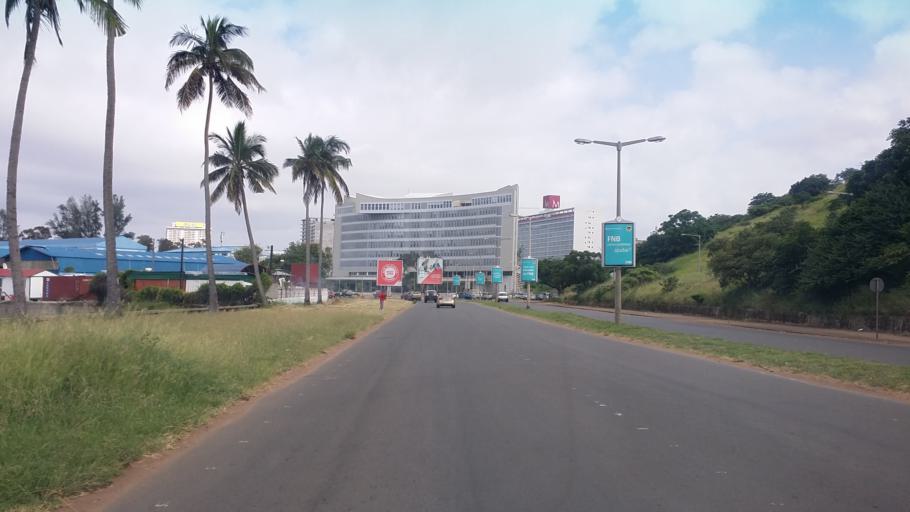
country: MZ
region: Maputo City
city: Maputo
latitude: -25.9823
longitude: 32.5865
